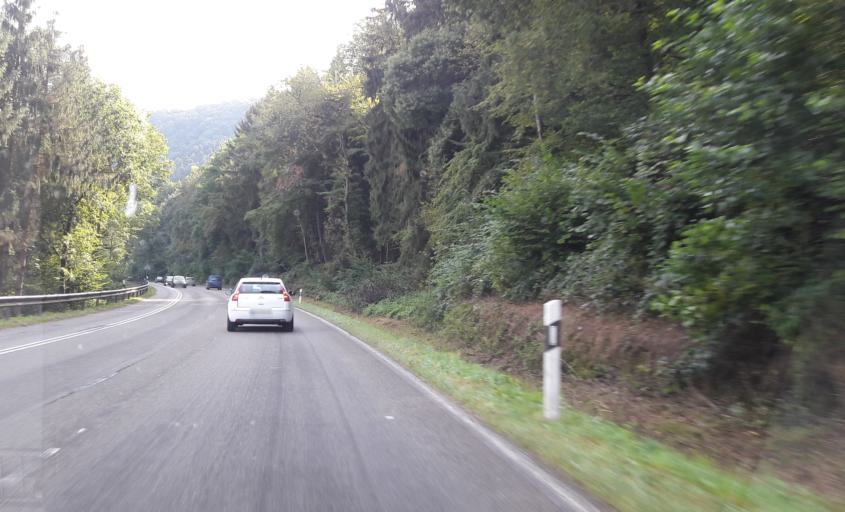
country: DE
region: Rheinland-Pfalz
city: Briedel
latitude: 50.0121
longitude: 7.1655
